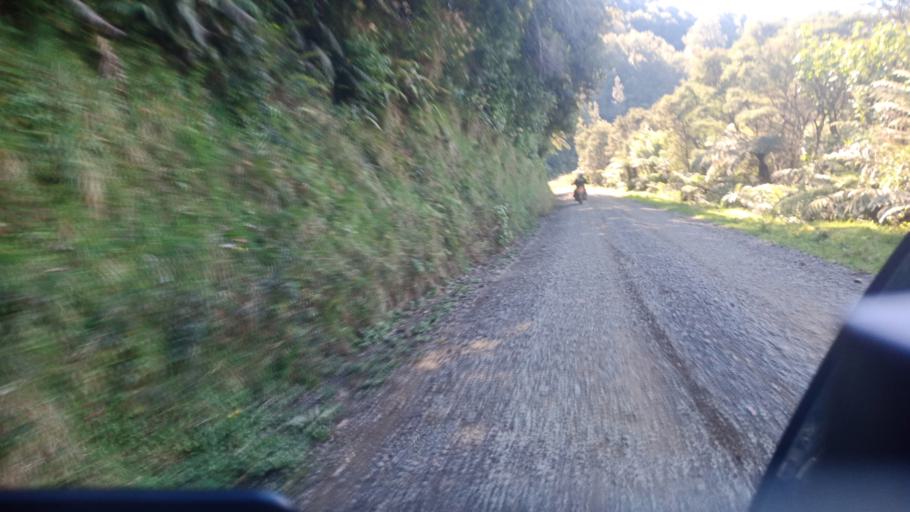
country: NZ
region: Bay of Plenty
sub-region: Opotiki District
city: Opotiki
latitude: -38.0381
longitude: 177.4415
